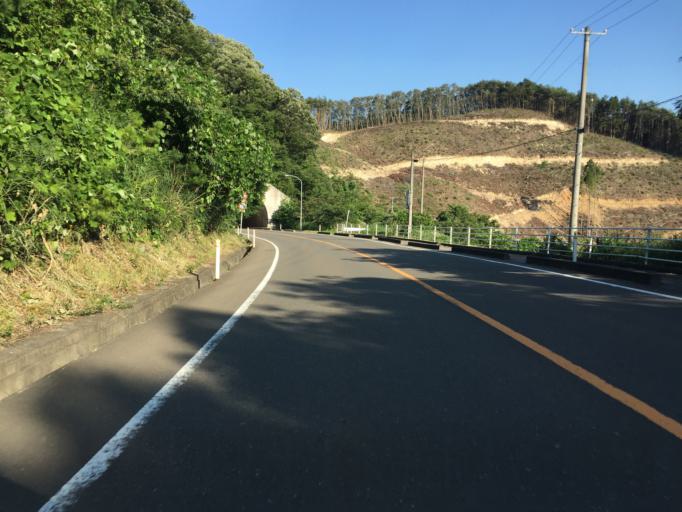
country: JP
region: Miyagi
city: Shiroishi
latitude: 37.9545
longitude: 140.5320
